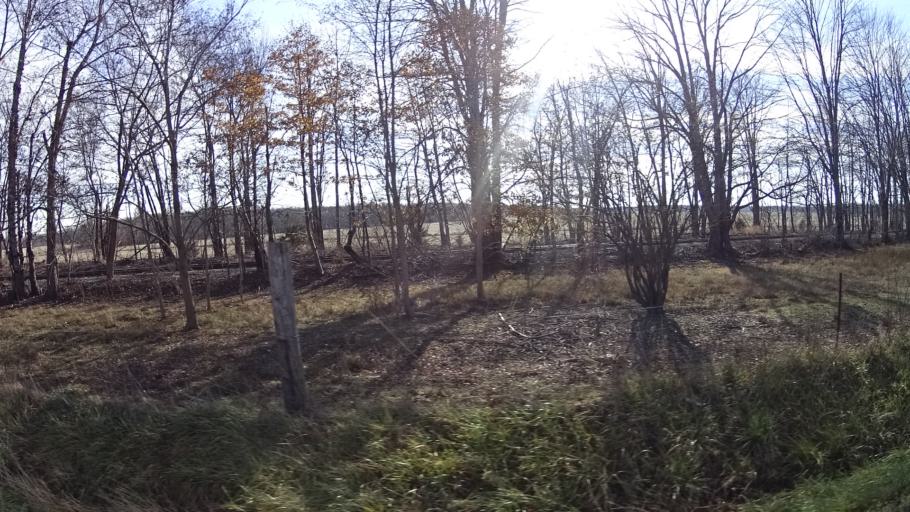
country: US
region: Ohio
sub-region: Lorain County
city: Wellington
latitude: 41.1002
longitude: -82.1728
